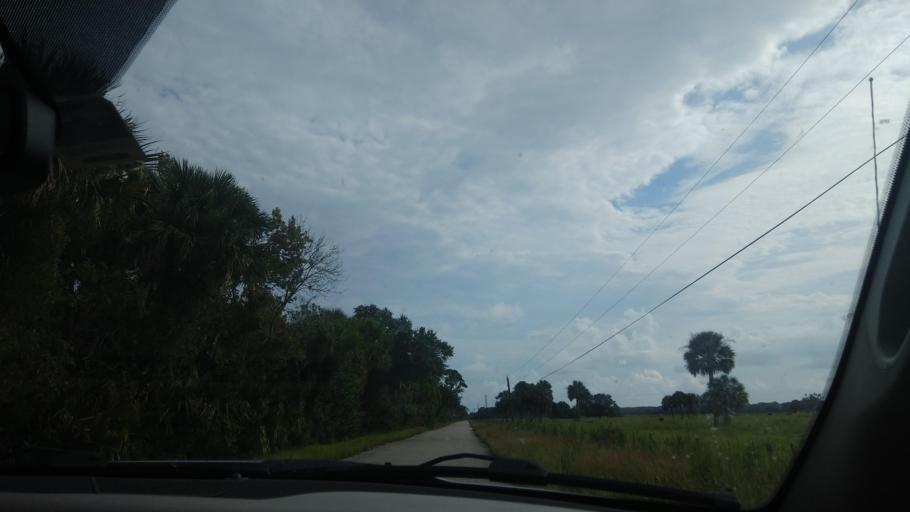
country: US
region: Florida
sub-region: Indian River County
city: Fellsmere
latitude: 27.6956
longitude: -80.7900
